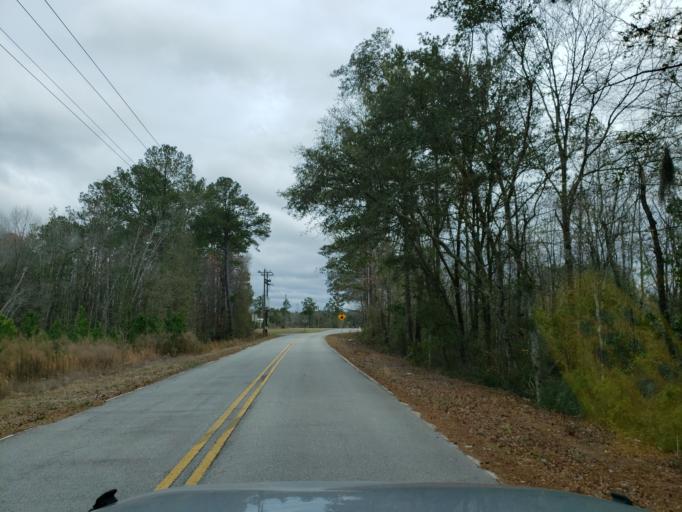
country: US
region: Georgia
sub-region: Chatham County
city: Bloomingdale
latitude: 32.0831
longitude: -81.3750
